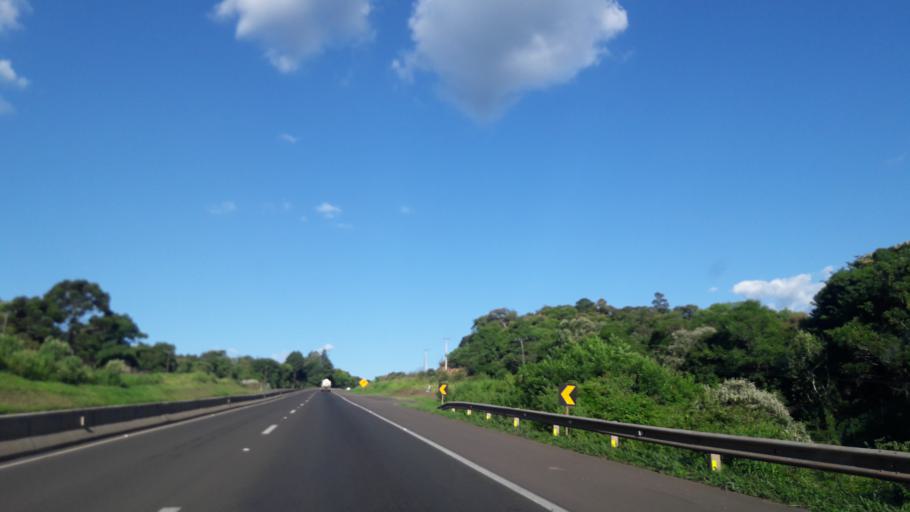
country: BR
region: Parana
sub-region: Guarapuava
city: Guarapuava
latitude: -25.3456
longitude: -51.4041
